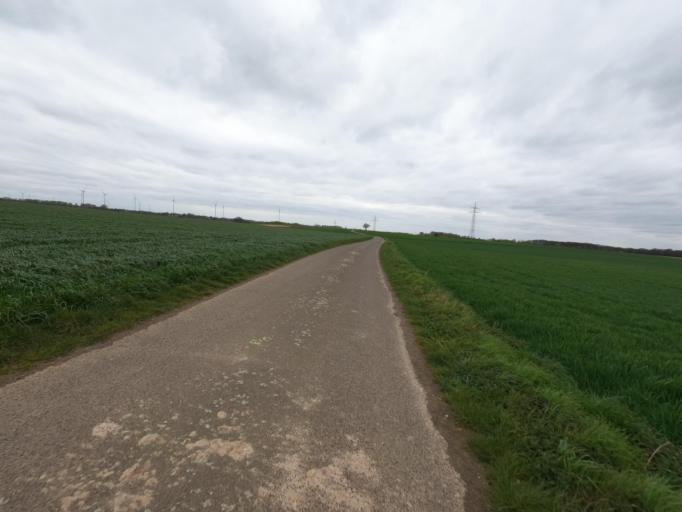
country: DE
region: North Rhine-Westphalia
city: Huckelhoven
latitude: 51.0140
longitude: 6.2020
